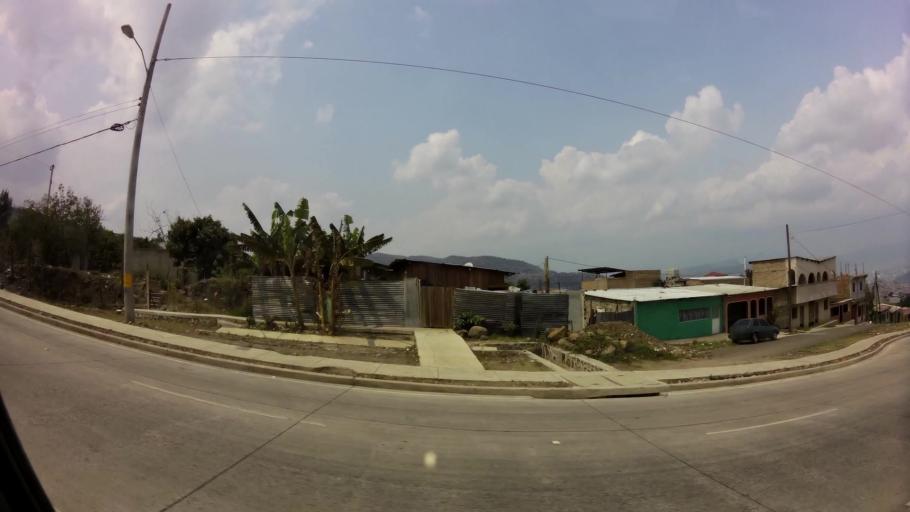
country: HN
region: Francisco Morazan
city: El Lolo
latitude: 14.0953
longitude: -87.2495
